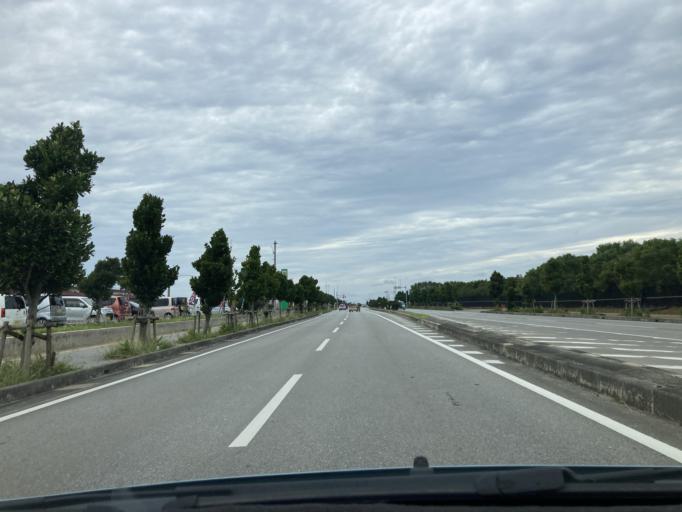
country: JP
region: Okinawa
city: Okinawa
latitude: 26.3934
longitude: 127.7458
